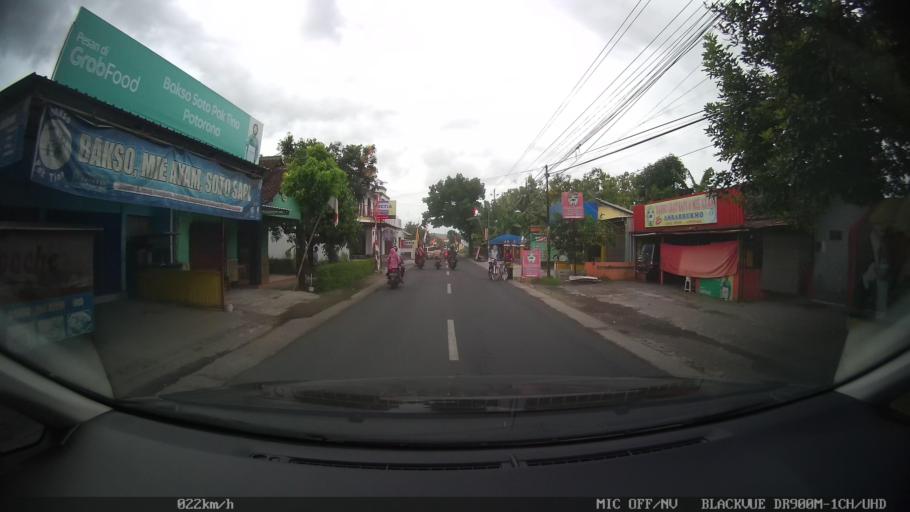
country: ID
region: Daerah Istimewa Yogyakarta
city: Sewon
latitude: -7.8578
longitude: 110.4092
